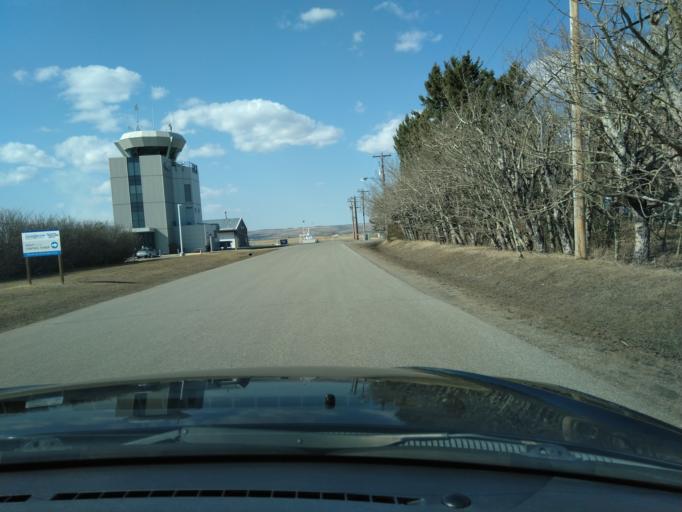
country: CA
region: Alberta
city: Cochrane
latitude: 51.1019
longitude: -114.3737
